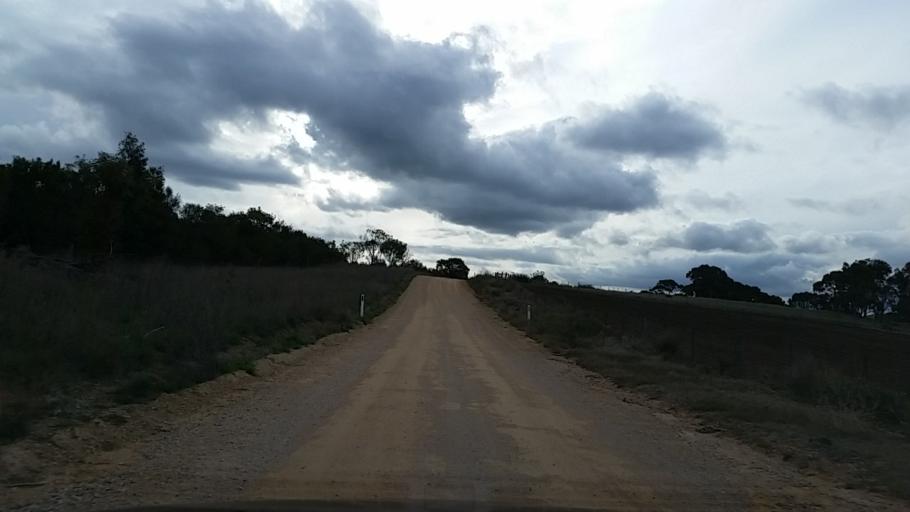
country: AU
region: South Australia
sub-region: Mount Barker
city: Nairne
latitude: -34.9779
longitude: 139.0332
